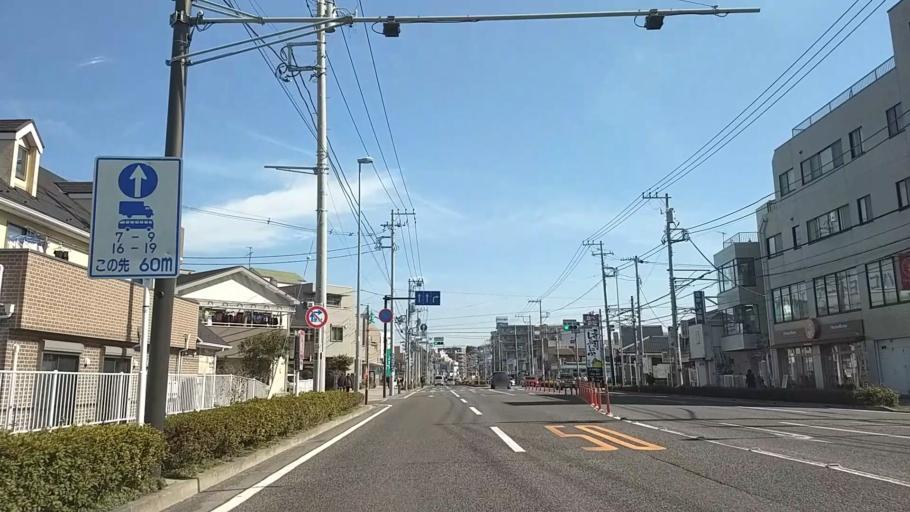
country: JP
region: Kanagawa
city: Kamakura
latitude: 35.3619
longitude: 139.5517
